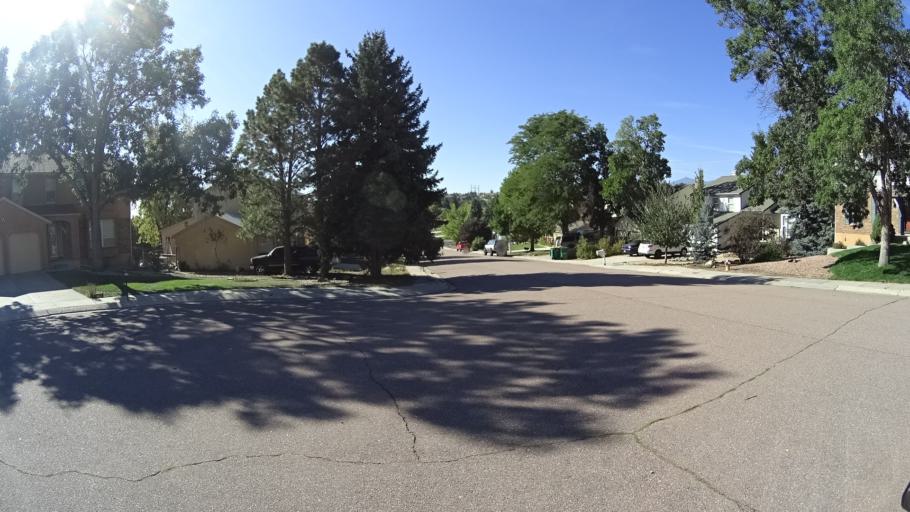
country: US
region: Colorado
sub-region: El Paso County
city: Colorado Springs
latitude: 38.9069
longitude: -104.7886
